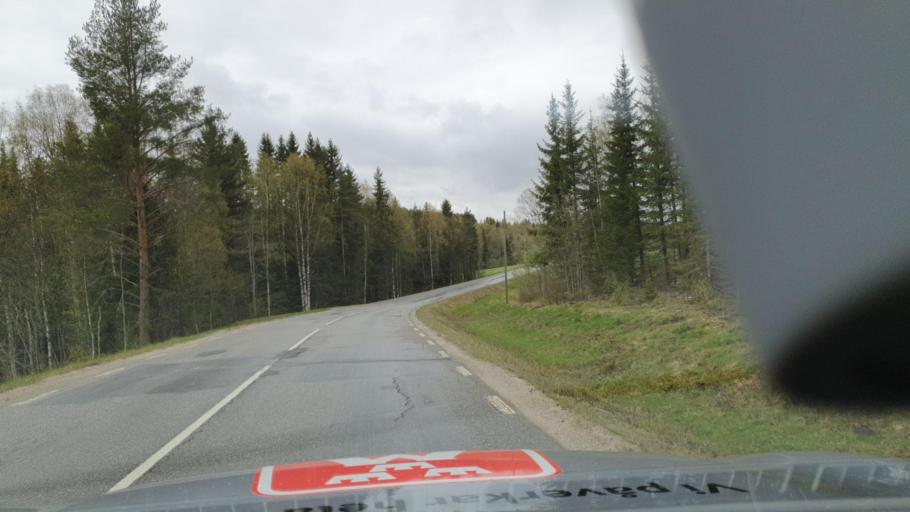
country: SE
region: Vaesternorrland
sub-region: OErnskoeldsviks Kommun
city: Bredbyn
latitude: 63.5284
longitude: 17.7259
